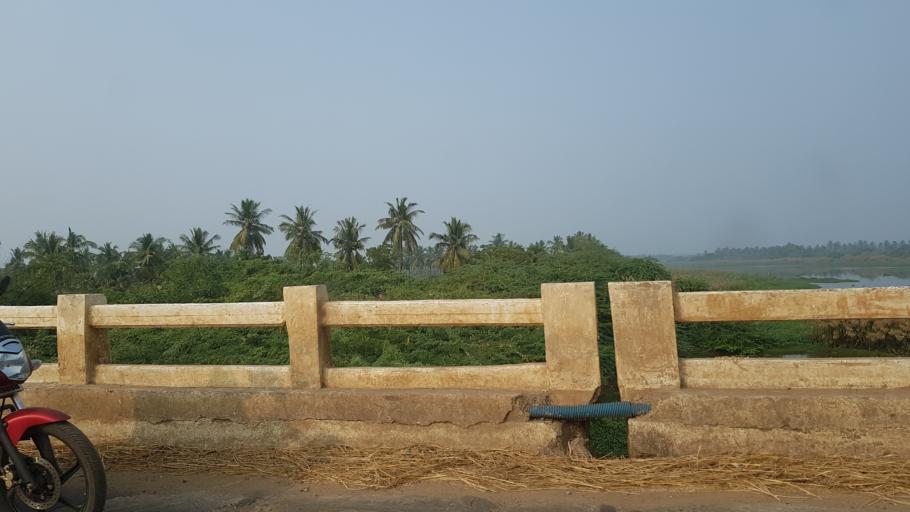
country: IN
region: Andhra Pradesh
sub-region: Krishna
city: Pallevada
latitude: 16.5197
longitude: 81.3366
